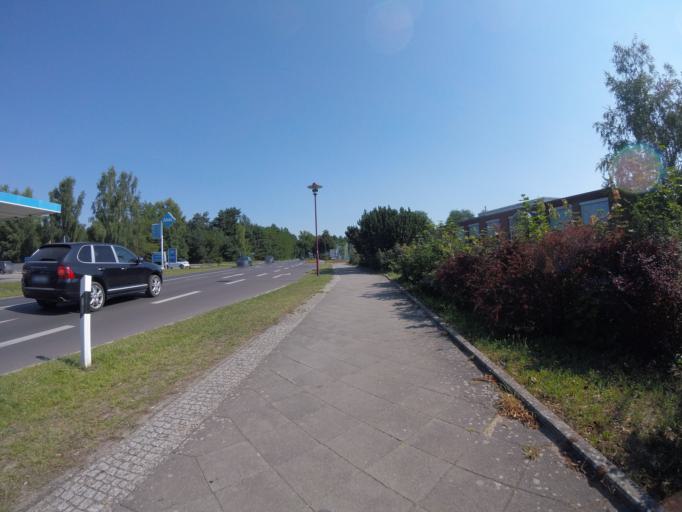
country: DE
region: Brandenburg
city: Mullrose
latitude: 52.2585
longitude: 14.4273
